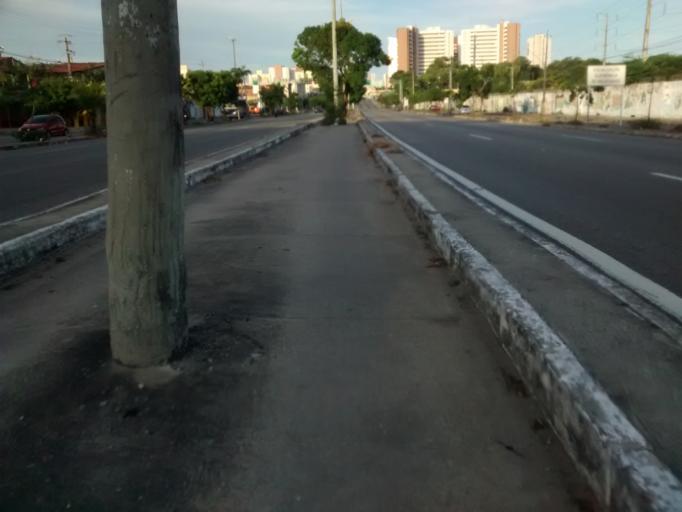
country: BR
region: Ceara
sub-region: Fortaleza
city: Fortaleza
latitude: -3.7374
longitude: -38.5754
